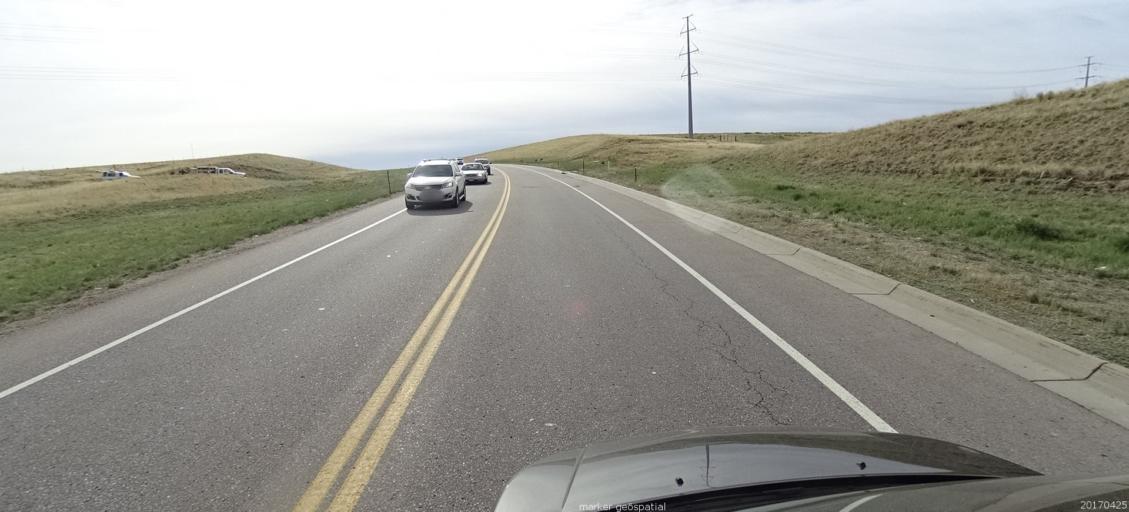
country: US
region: Colorado
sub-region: Douglas County
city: Meridian
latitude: 39.5198
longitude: -104.8492
